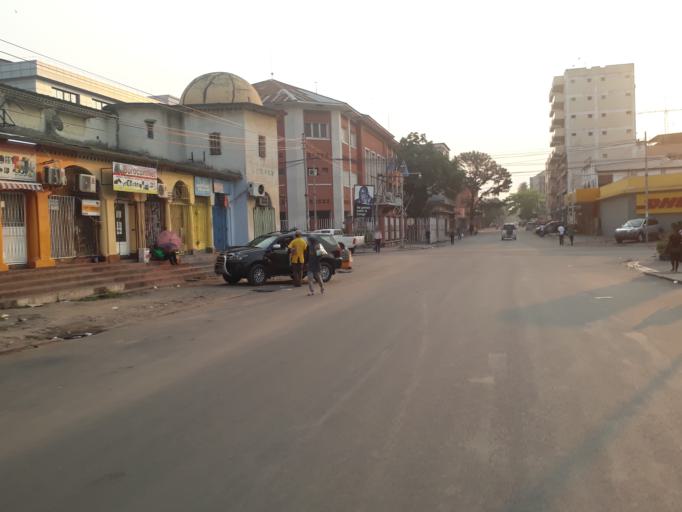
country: CD
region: Kinshasa
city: Kinshasa
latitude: -4.3057
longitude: 15.3091
